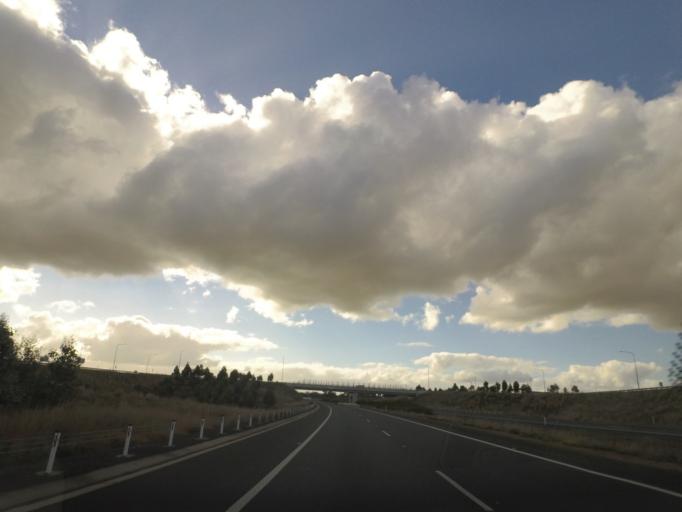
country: AU
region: New South Wales
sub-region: Greater Hume Shire
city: Holbrook
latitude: -35.7343
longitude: 147.3054
